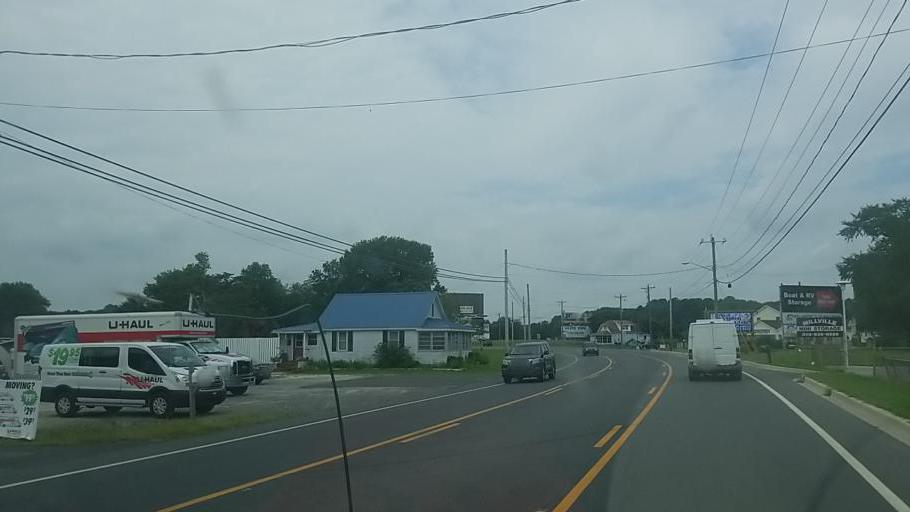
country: US
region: Delaware
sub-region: Sussex County
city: Ocean View
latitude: 38.5505
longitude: -75.1251
